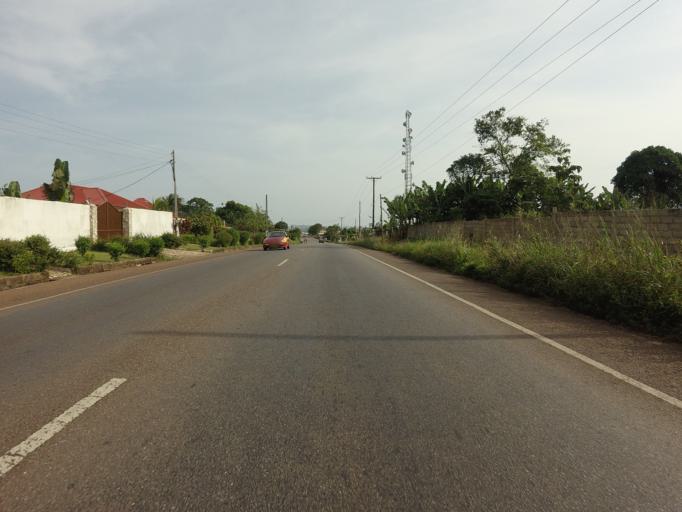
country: GH
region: Eastern
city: Aburi
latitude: 5.8593
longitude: -0.1663
